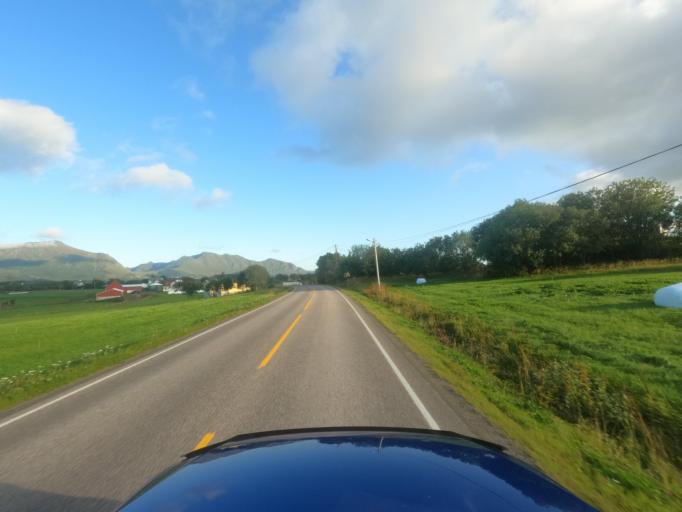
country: NO
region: Nordland
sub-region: Vestvagoy
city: Gravdal
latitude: 68.1380
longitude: 13.5552
